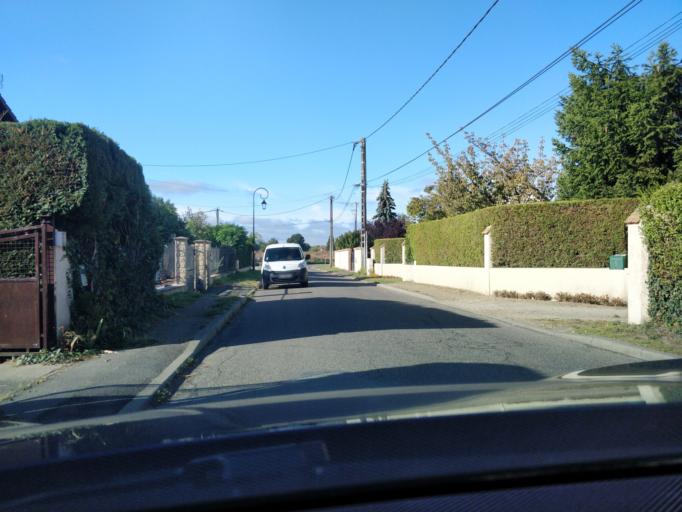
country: FR
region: Ile-de-France
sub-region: Departement de l'Essonne
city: Forges-les-Bains
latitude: 48.6039
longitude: 2.0950
